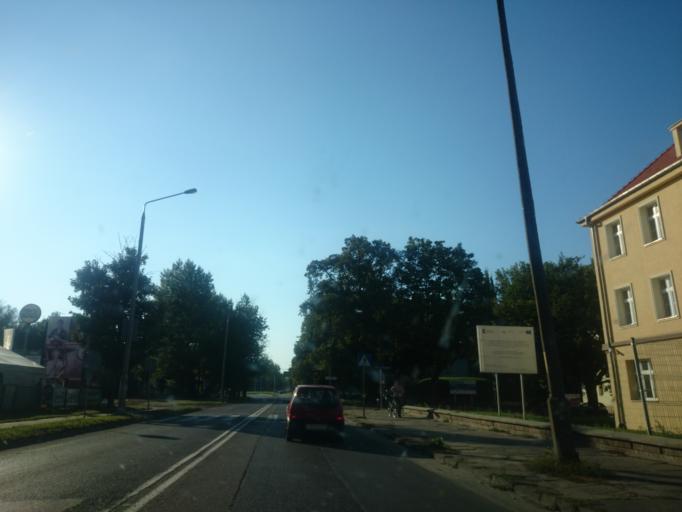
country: PL
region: Lubusz
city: Gorzow Wielkopolski
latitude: 52.7362
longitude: 15.2043
